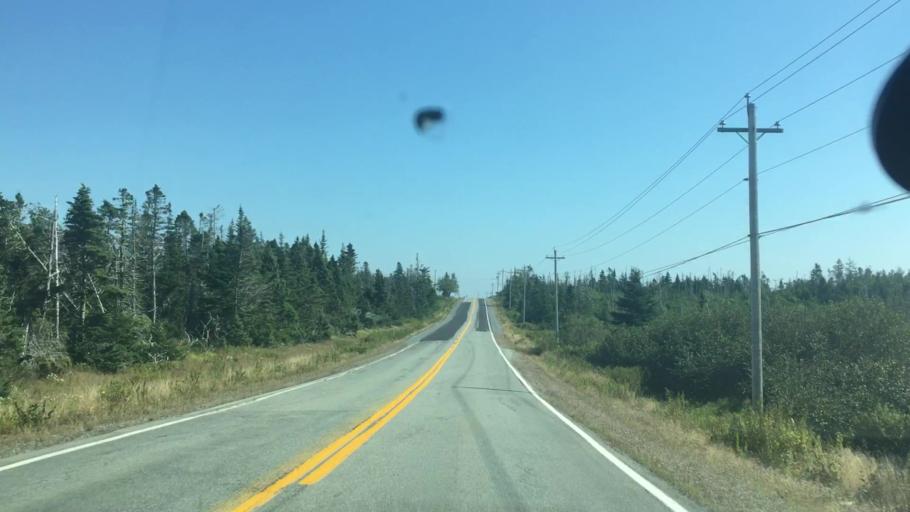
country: CA
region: Nova Scotia
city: New Glasgow
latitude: 44.9162
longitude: -62.3134
